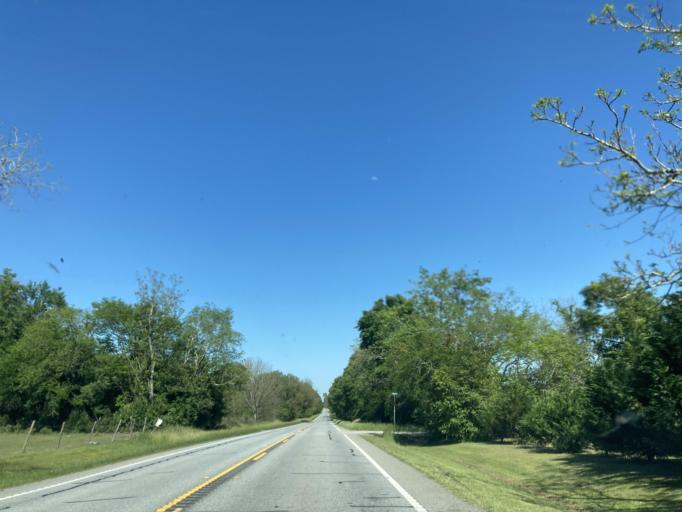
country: US
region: Georgia
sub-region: Miller County
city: Colquitt
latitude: 31.1853
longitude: -84.5341
